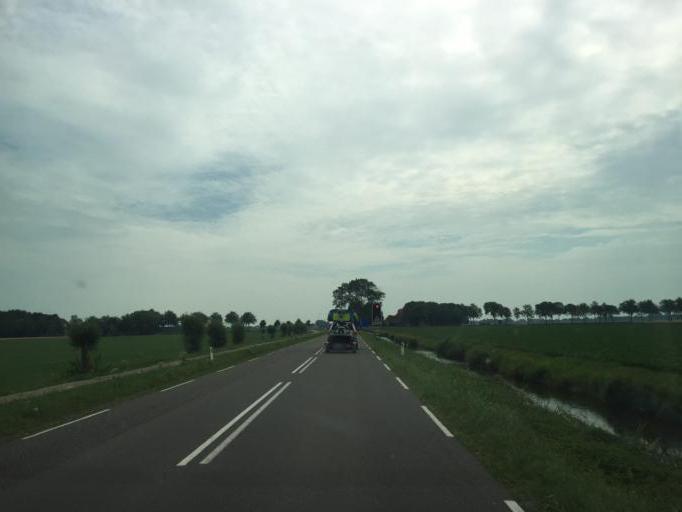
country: NL
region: North Holland
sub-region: Gemeente Beemster
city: Halfweg
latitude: 52.5948
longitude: 4.9055
